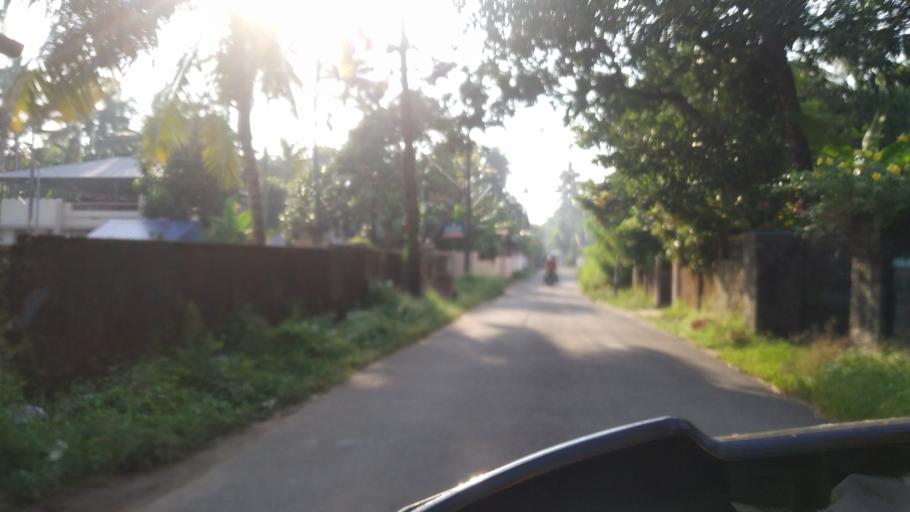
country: IN
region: Kerala
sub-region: Ernakulam
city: Elur
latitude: 10.0463
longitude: 76.2230
